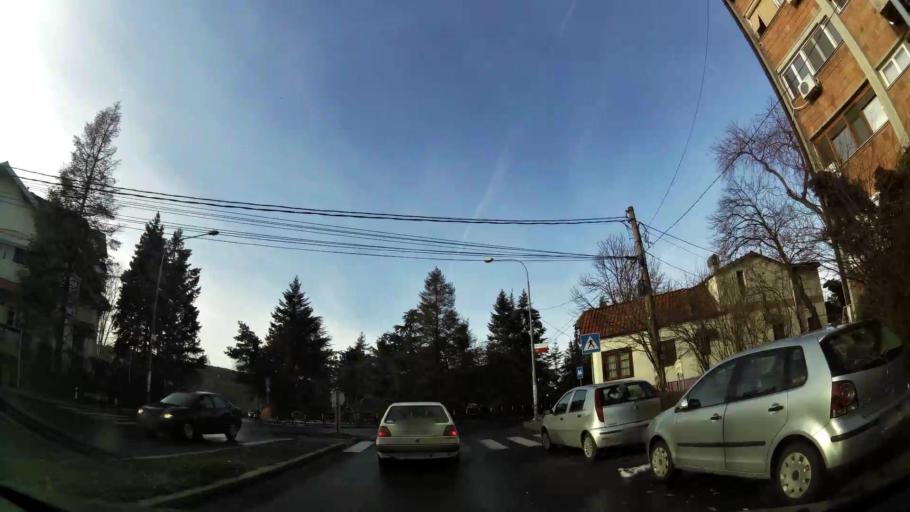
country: RS
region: Central Serbia
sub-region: Belgrade
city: Rakovica
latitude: 44.7525
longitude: 20.4508
